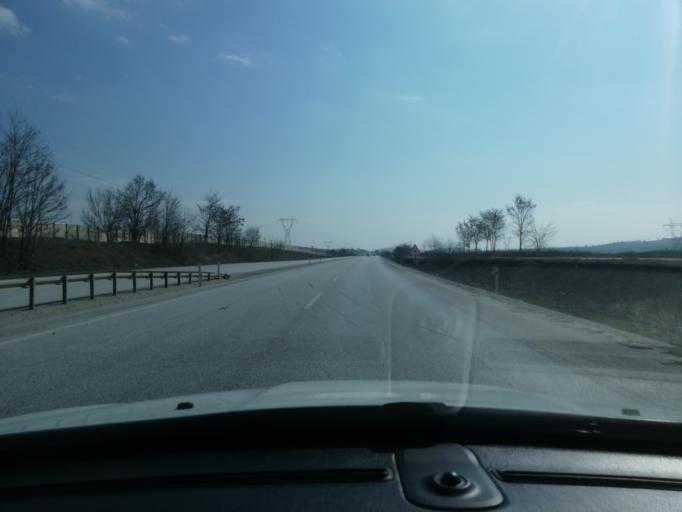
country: TR
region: Cankiri
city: Kursunlu
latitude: 40.8419
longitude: 33.1689
